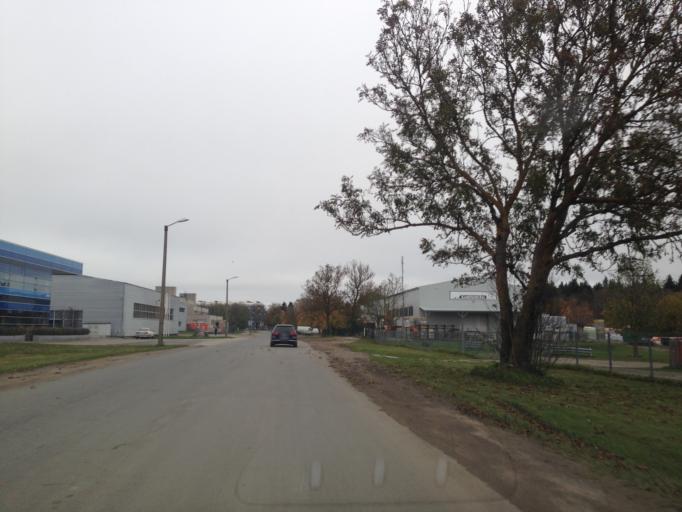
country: EE
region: Harju
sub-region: Harku vald
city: Tabasalu
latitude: 59.4233
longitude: 24.5409
